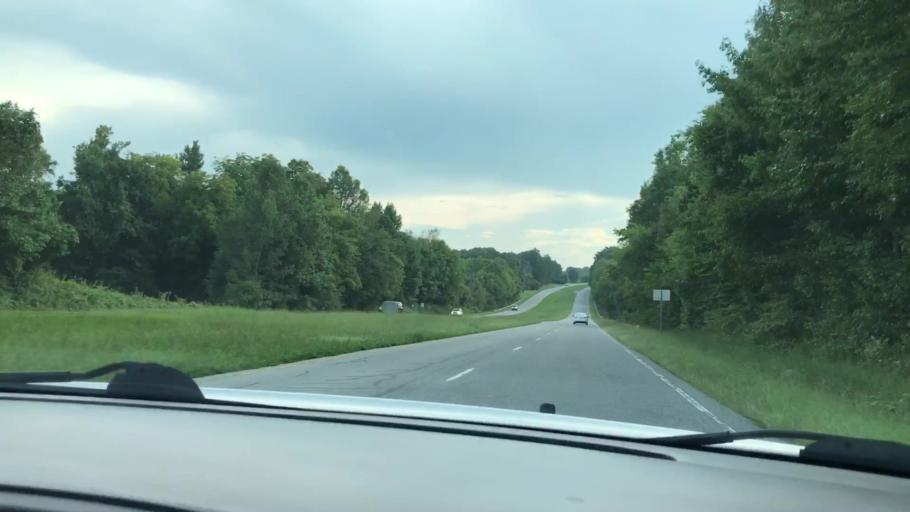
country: US
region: North Carolina
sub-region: Davidson County
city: Denton
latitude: 35.6044
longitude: -80.0271
